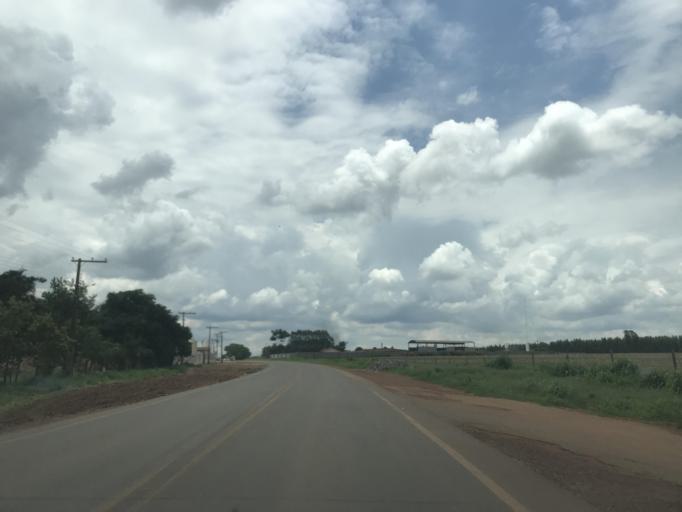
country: BR
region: Goias
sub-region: Vianopolis
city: Vianopolis
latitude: -16.7362
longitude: -48.4865
